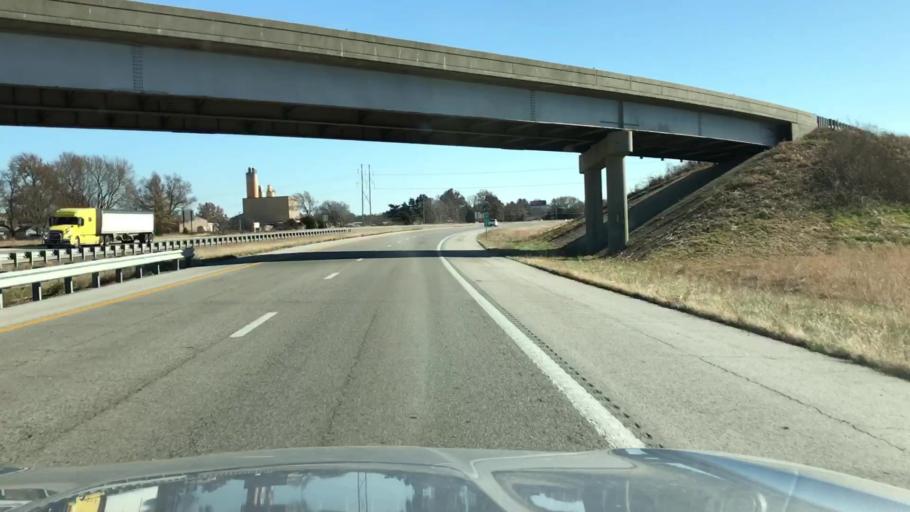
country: US
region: Missouri
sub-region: Jasper County
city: Carthage
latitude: 37.1331
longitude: -94.3140
